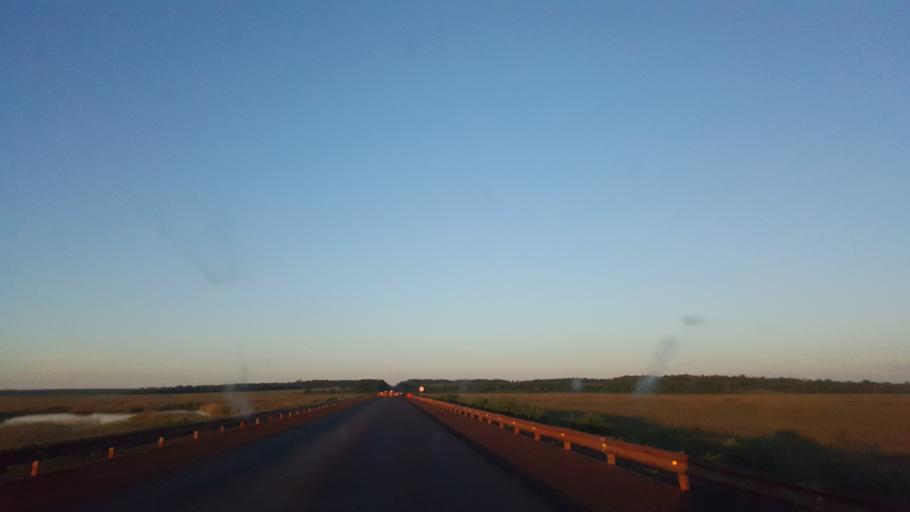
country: AR
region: Corrientes
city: Santo Tome
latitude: -28.3851
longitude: -55.9636
